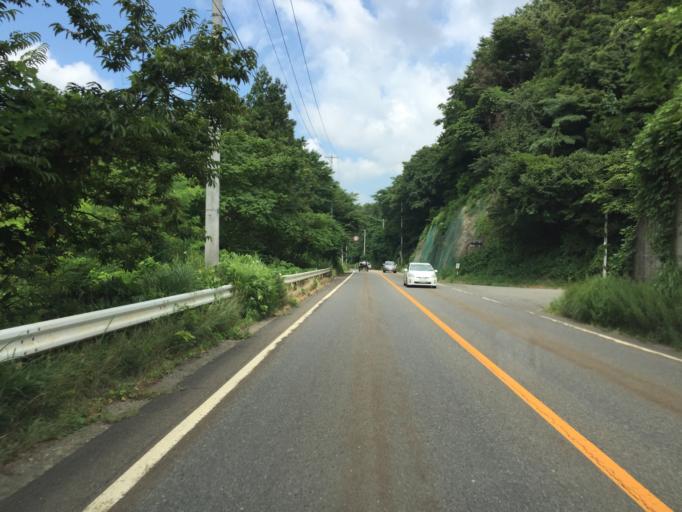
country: JP
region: Fukushima
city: Inawashiro
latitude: 37.4944
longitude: 140.2196
